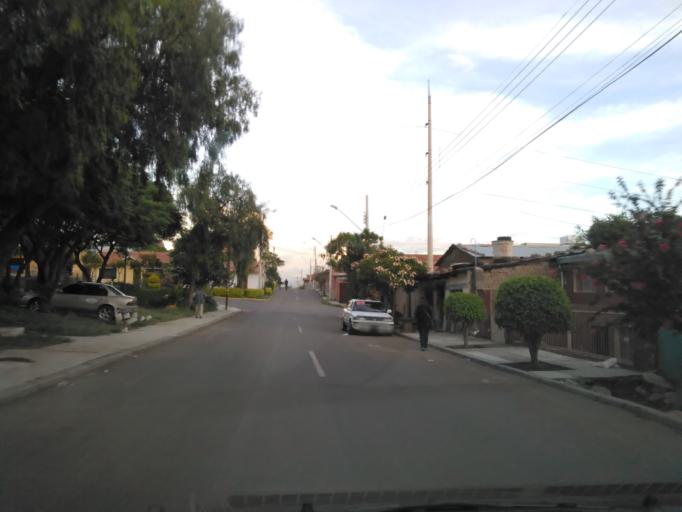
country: BO
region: Cochabamba
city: Cochabamba
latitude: -17.3621
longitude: -66.1603
